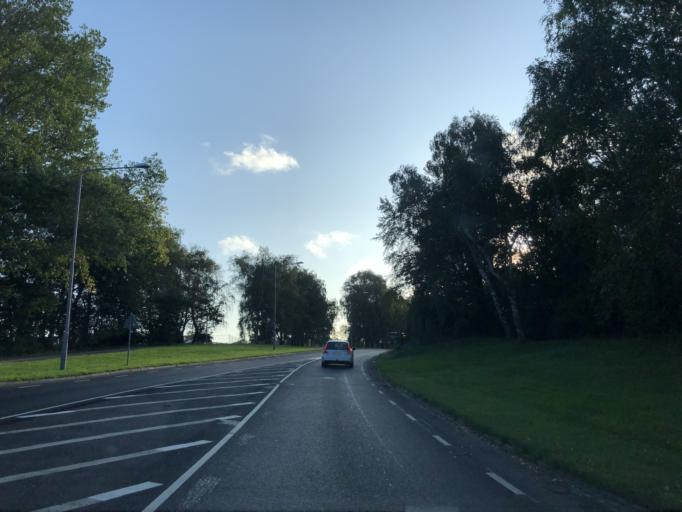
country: SE
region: Vaestra Goetaland
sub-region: Goteborg
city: Majorna
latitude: 57.6477
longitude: 11.8814
